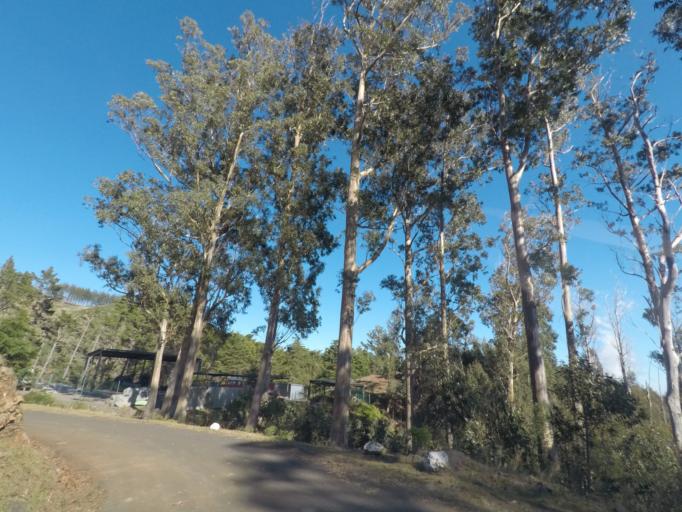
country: PT
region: Madeira
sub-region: Funchal
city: Nossa Senhora do Monte
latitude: 32.6997
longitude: -16.9062
